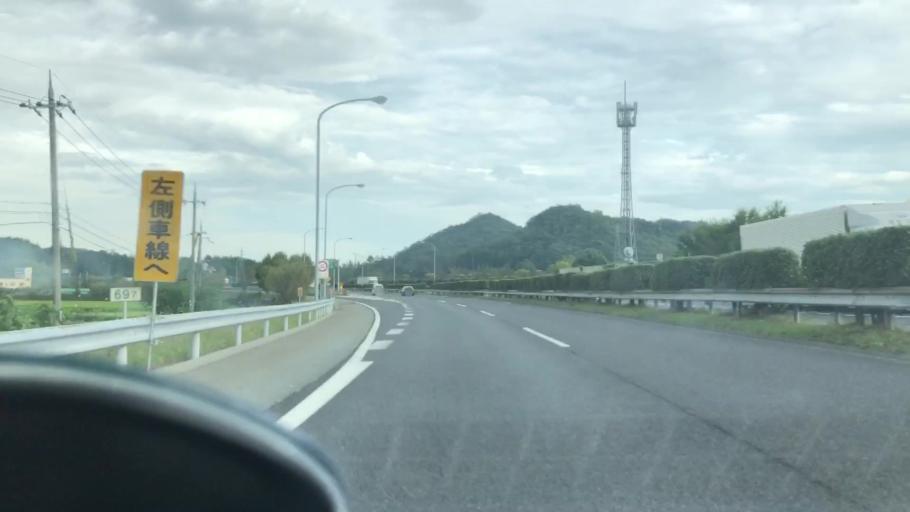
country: JP
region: Hyogo
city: Yashiro
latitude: 34.9348
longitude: 134.8616
